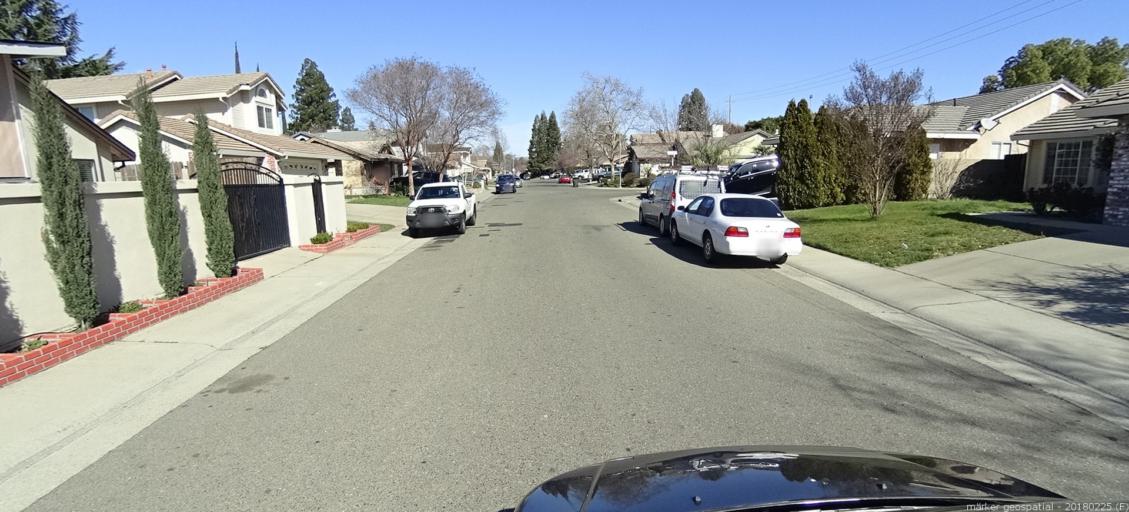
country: US
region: California
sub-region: Sacramento County
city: North Highlands
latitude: 38.7186
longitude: -121.3931
